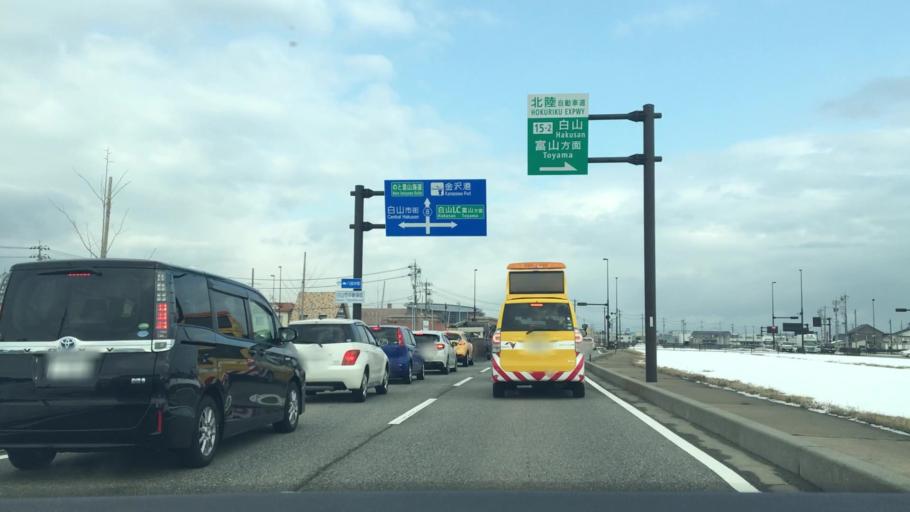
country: JP
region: Ishikawa
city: Matsuto
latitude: 36.5562
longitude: 136.5795
